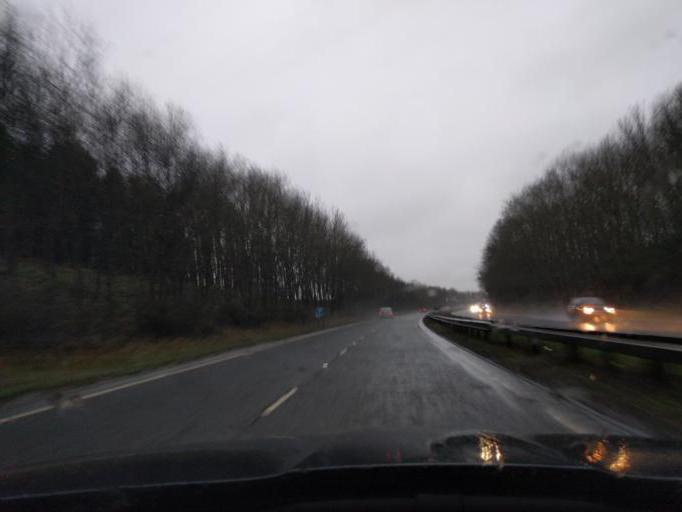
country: GB
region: England
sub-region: Northumberland
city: Bedlington
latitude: 55.1215
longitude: -1.5542
